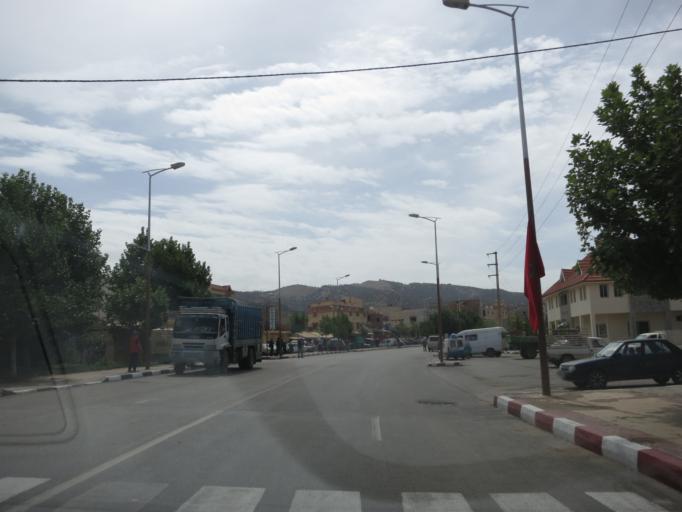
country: MA
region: Meknes-Tafilalet
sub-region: Ifrane
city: Azrou
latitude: 33.2368
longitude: -5.0594
